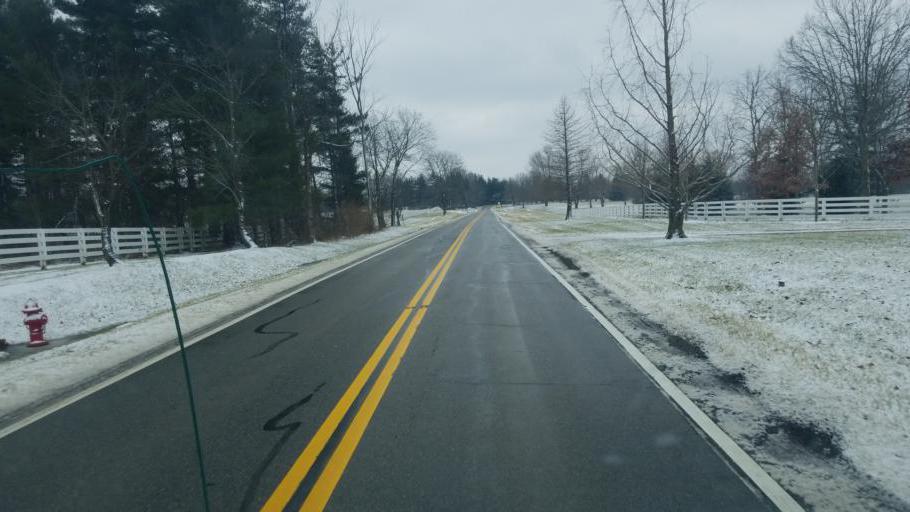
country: US
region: Ohio
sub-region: Franklin County
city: New Albany
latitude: 40.0764
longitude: -82.7913
